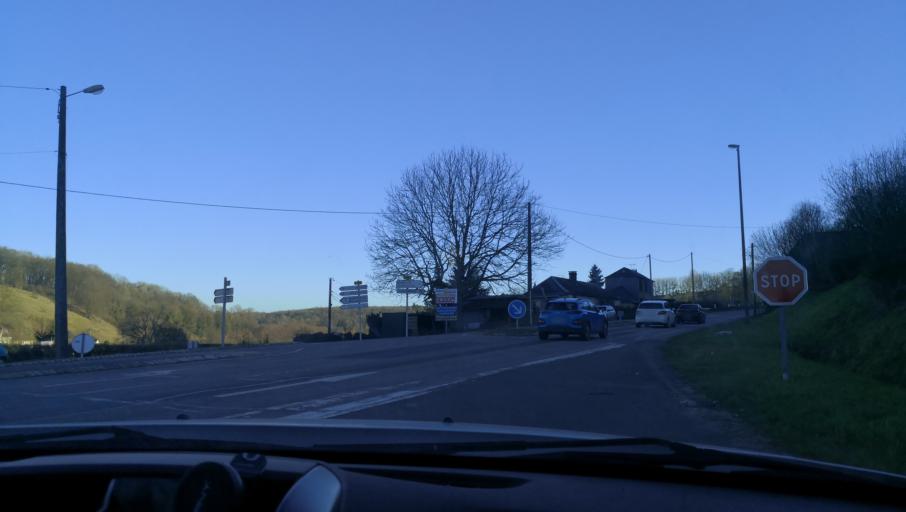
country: FR
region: Haute-Normandie
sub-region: Departement de la Seine-Maritime
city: Saint-Martin-Osmonville
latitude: 49.6451
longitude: 1.3019
